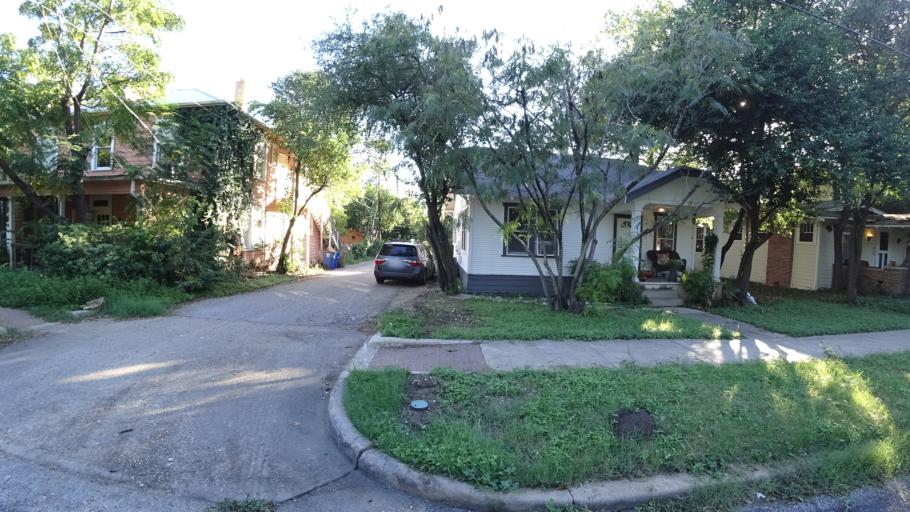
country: US
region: Texas
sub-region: Travis County
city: Austin
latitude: 30.2990
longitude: -97.7304
